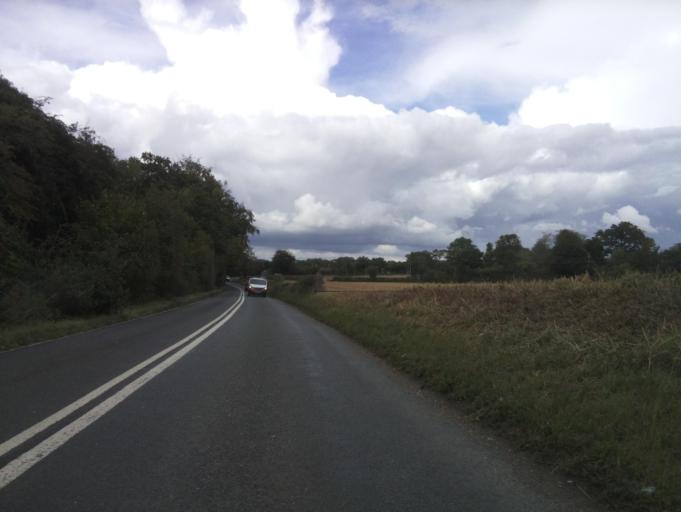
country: GB
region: England
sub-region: Staffordshire
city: Gnosall
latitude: 52.8167
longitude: -2.3118
